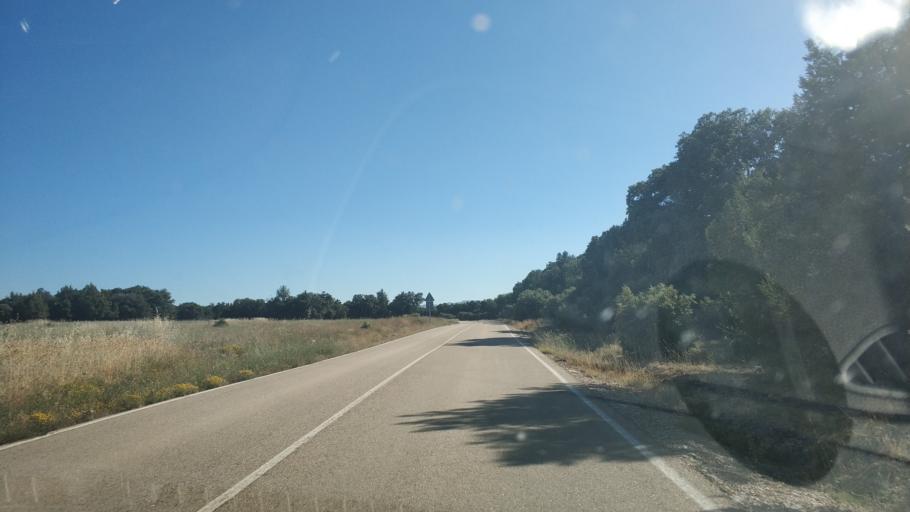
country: ES
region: Castille and Leon
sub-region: Provincia de Soria
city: Liceras
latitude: 41.4530
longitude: -3.2131
